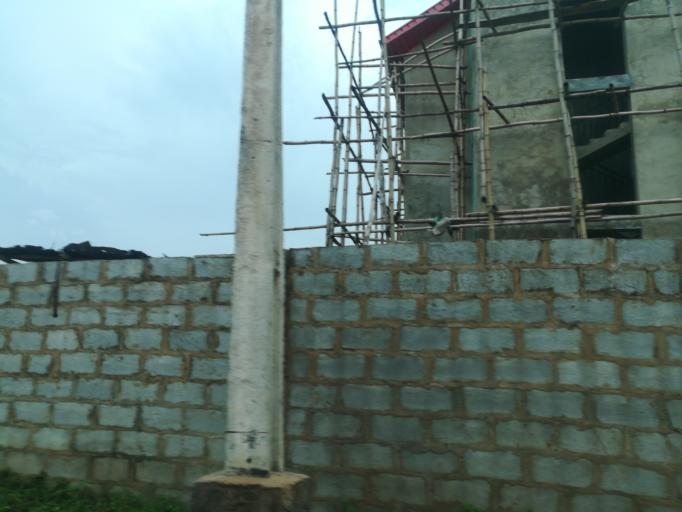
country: NG
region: Oyo
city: Ibadan
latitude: 7.4465
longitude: 3.9170
